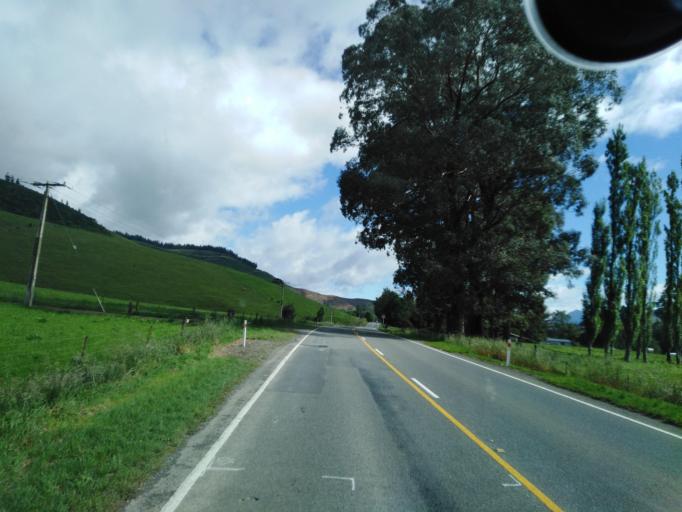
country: NZ
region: Nelson
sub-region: Nelson City
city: Nelson
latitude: -41.2772
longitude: 173.5733
